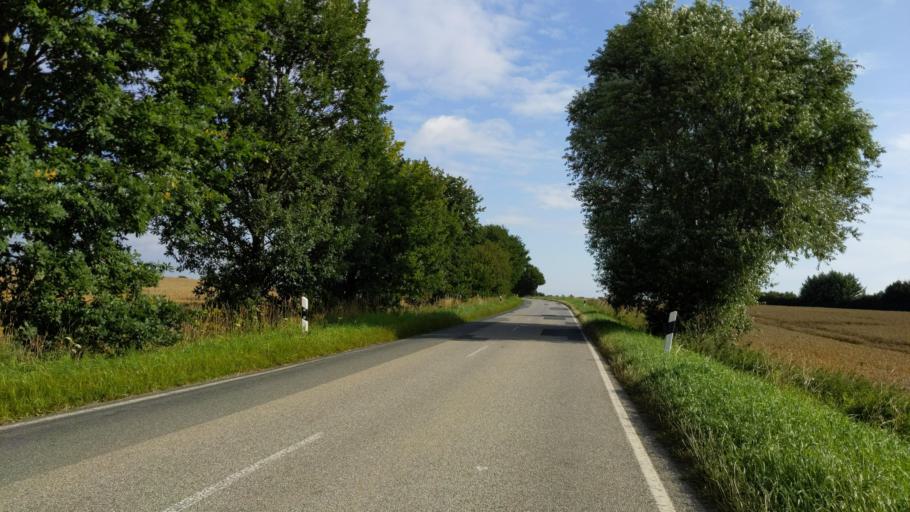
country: DE
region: Schleswig-Holstein
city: Bad Schwartau
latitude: 53.9832
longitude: 10.6595
